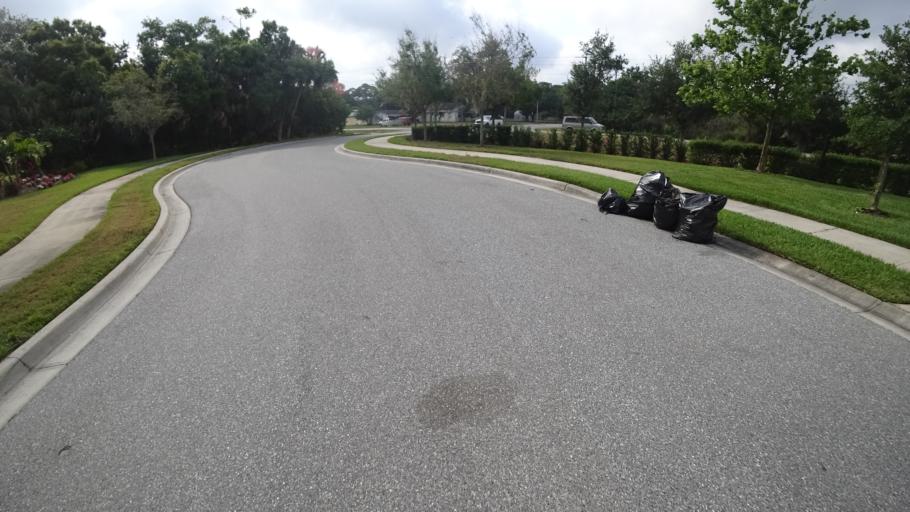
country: US
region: Florida
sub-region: Manatee County
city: Samoset
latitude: 27.4294
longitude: -82.5181
